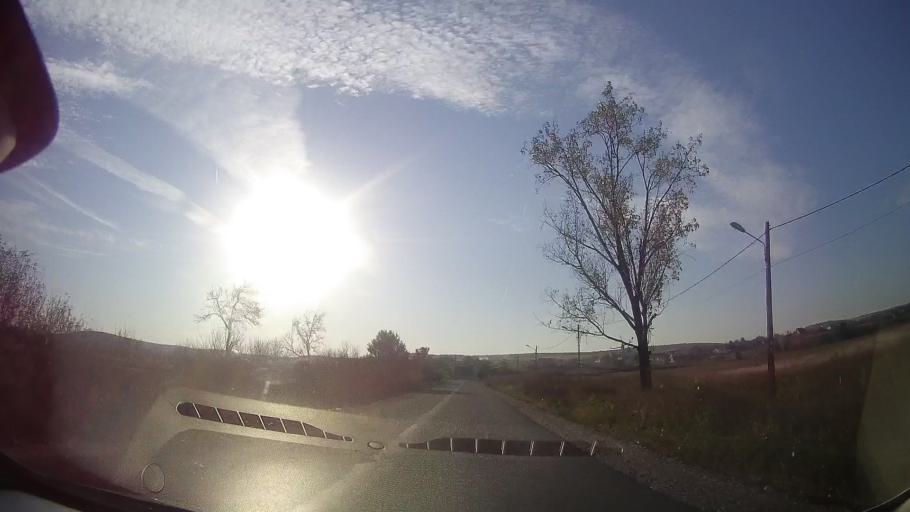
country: RO
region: Timis
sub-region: Comuna Masloc
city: Masloc
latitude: 45.9709
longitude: 21.4739
